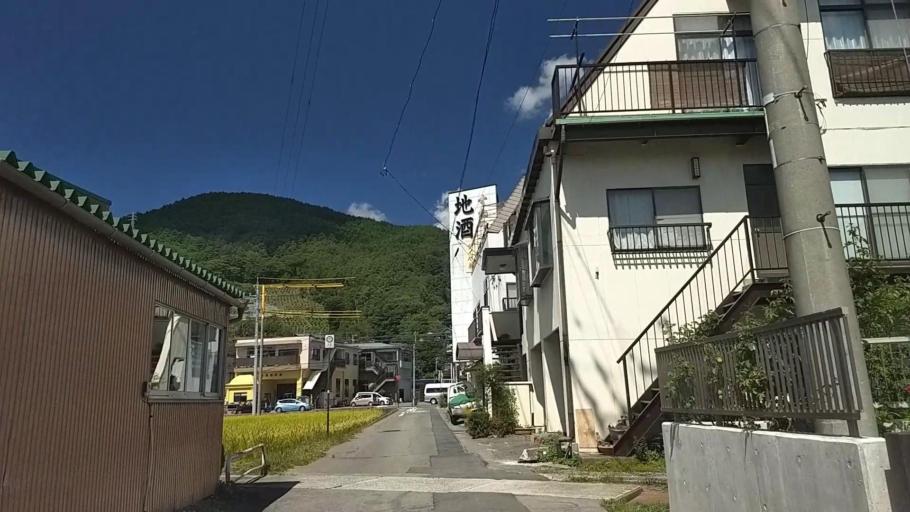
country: JP
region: Nagano
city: Chino
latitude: 35.9987
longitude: 138.1555
